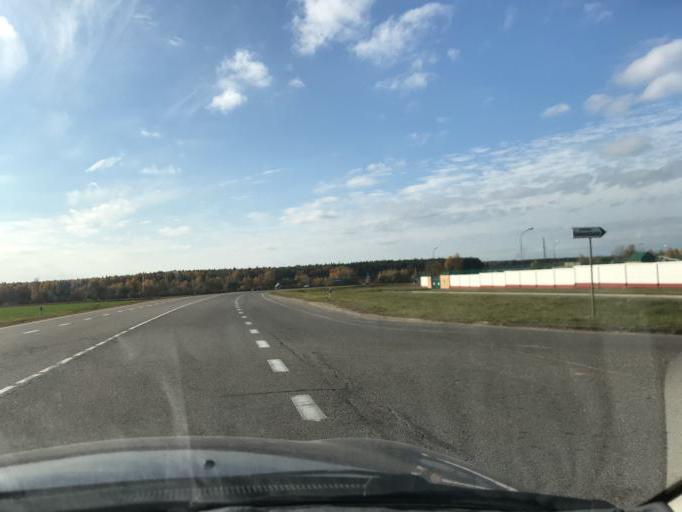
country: BY
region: Grodnenskaya
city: Voranava
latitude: 54.1418
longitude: 25.3223
